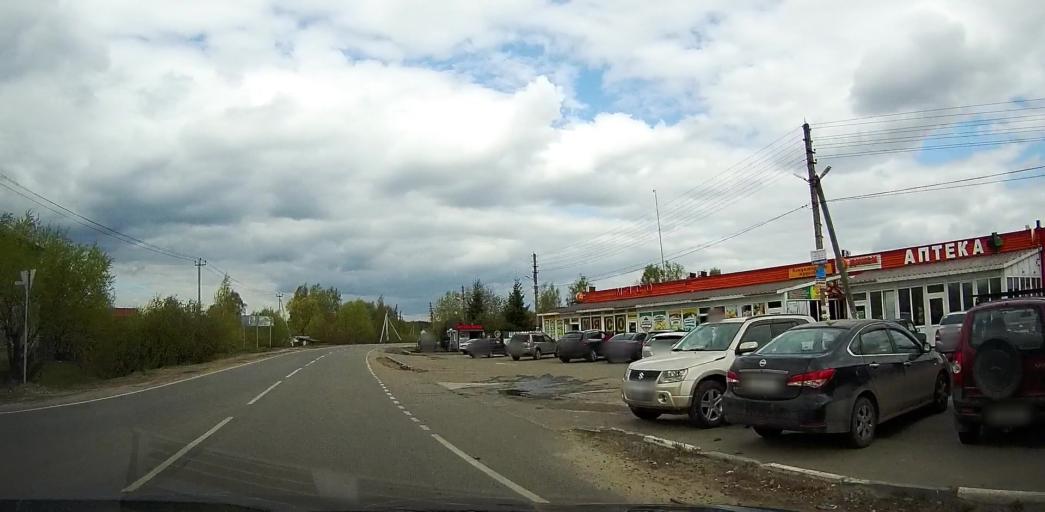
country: RU
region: Moskovskaya
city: Ashitkovo
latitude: 55.4265
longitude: 38.5791
